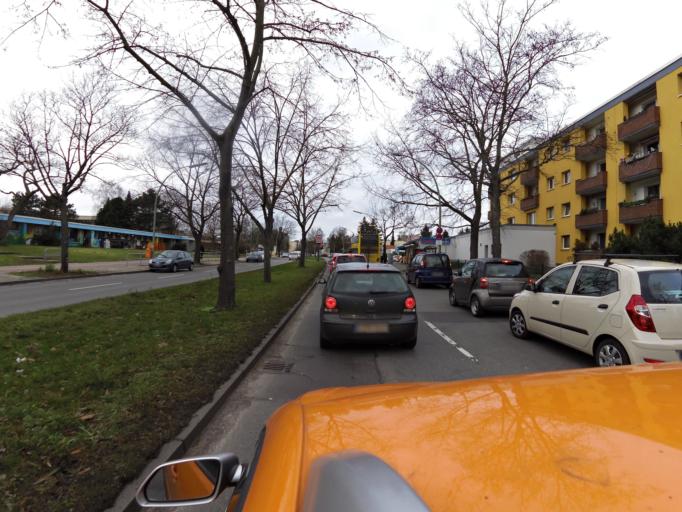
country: DE
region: Berlin
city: Gropiusstadt
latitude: 52.4292
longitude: 13.4659
